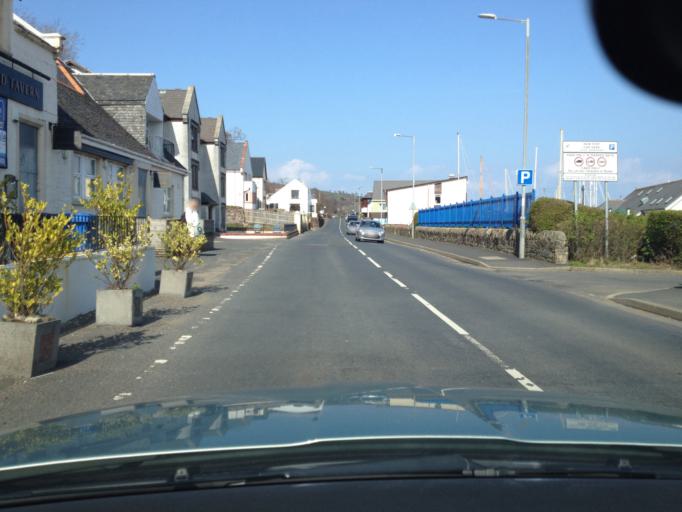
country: GB
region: Scotland
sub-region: North Ayrshire
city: Lamlash
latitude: 55.5349
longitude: -5.1260
